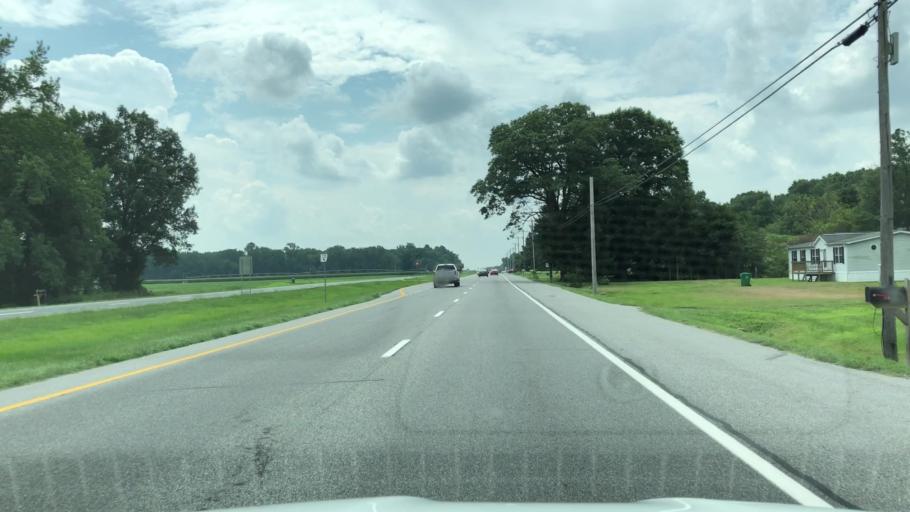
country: US
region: Delaware
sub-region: Kent County
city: Felton
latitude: 39.0194
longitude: -75.5655
